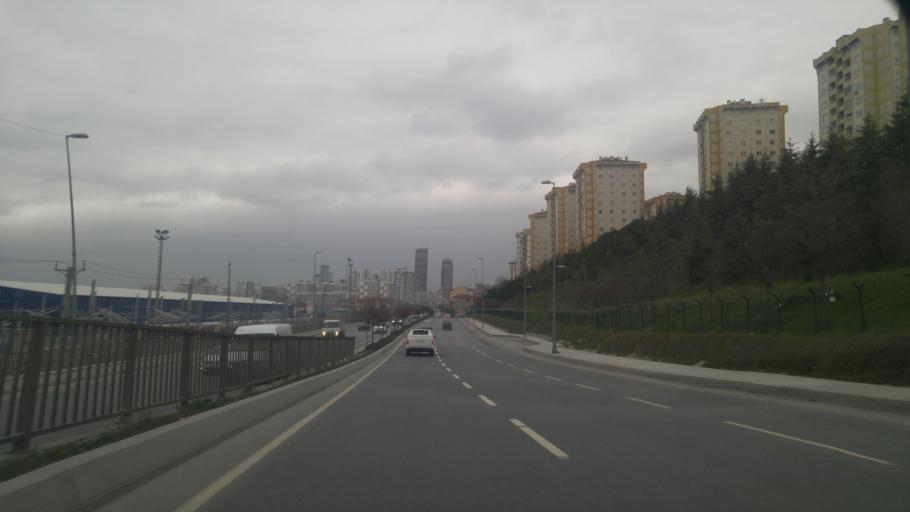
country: TR
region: Istanbul
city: Mahmutbey
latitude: 41.0252
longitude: 28.7676
